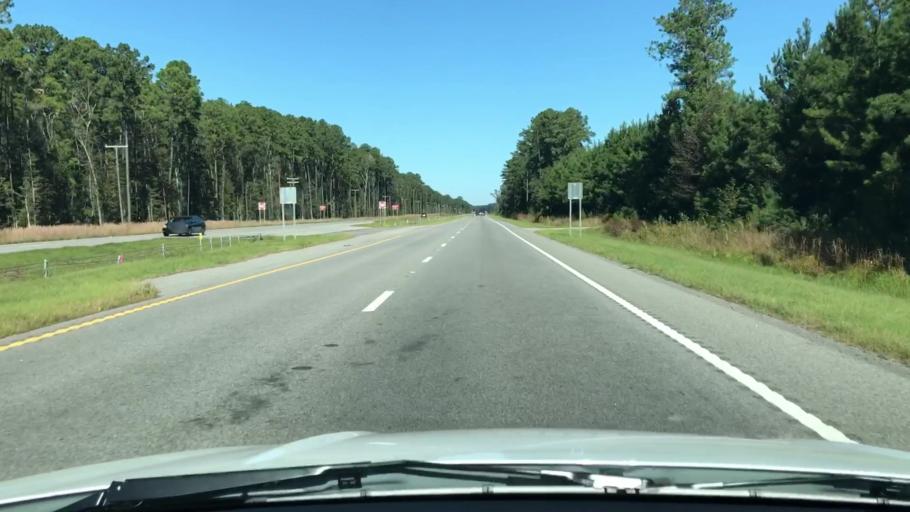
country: US
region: South Carolina
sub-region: Colleton County
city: Walterboro
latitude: 32.6956
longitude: -80.6237
